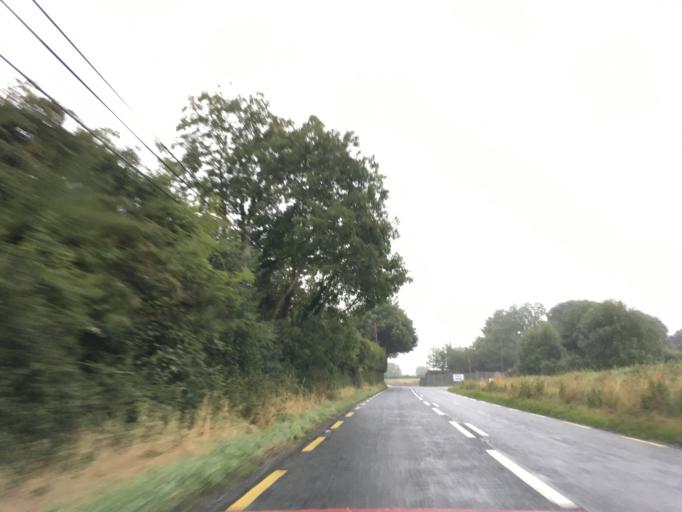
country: IE
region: Munster
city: Tipperary
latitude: 52.4828
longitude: -8.0854
